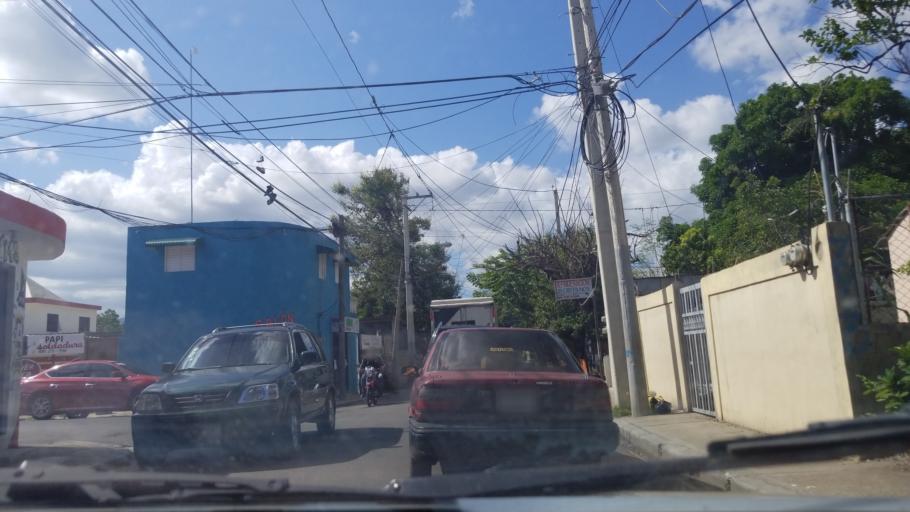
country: DO
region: Santiago
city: Santiago de los Caballeros
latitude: 19.4824
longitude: -70.6874
